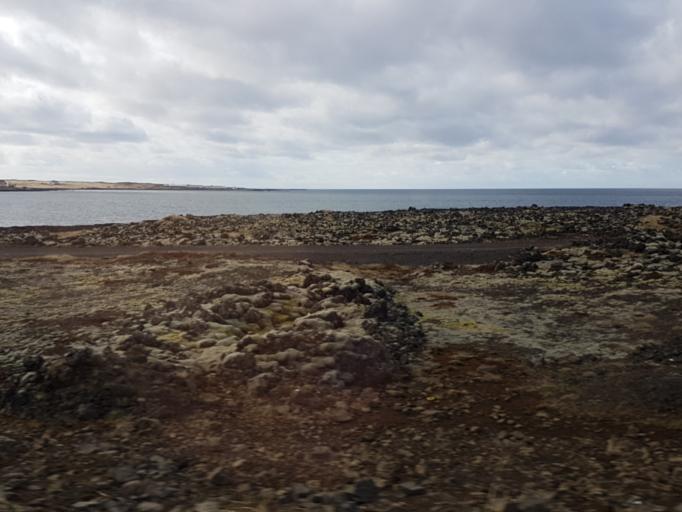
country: IS
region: Capital Region
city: Alftanes
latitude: 64.0151
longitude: -22.1787
